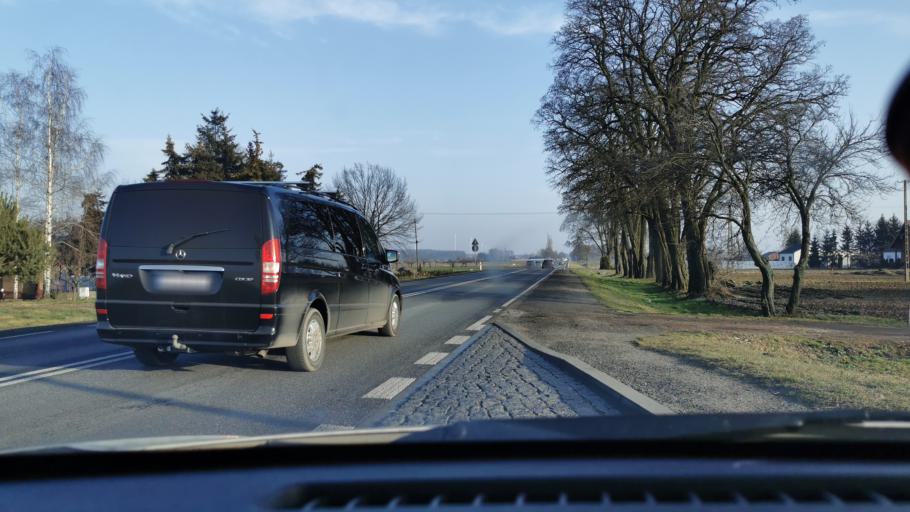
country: PL
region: Lodz Voivodeship
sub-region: Powiat sieradzki
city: Blaszki
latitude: 51.6439
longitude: 18.4820
